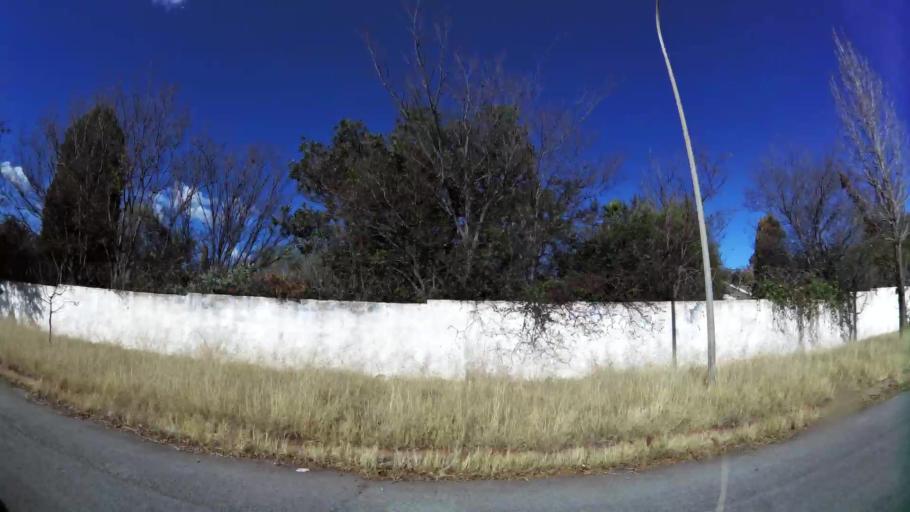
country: ZA
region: Gauteng
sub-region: West Rand District Municipality
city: Carletonville
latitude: -26.3667
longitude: 27.3668
